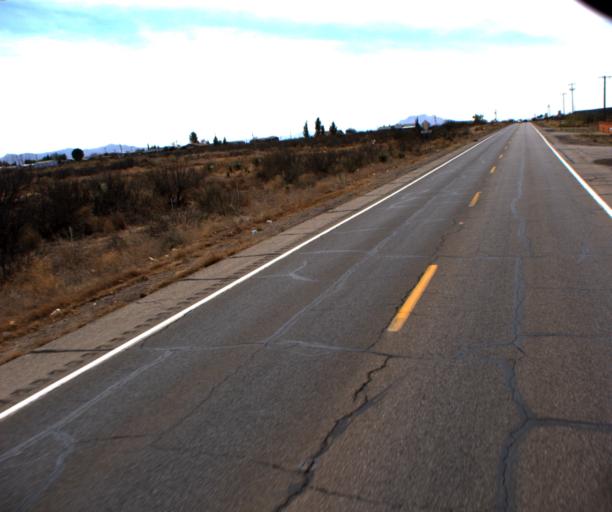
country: US
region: Arizona
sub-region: Cochise County
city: Pirtleville
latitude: 31.3618
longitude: -109.5794
